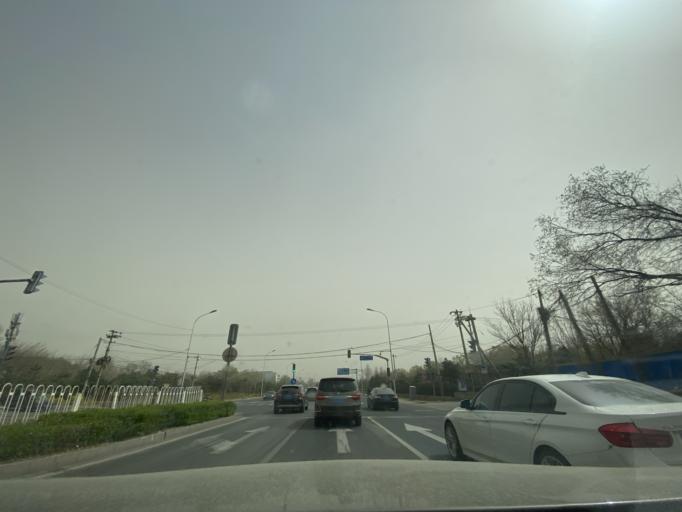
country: CN
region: Beijing
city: Sijiqing
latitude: 39.9456
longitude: 116.2592
